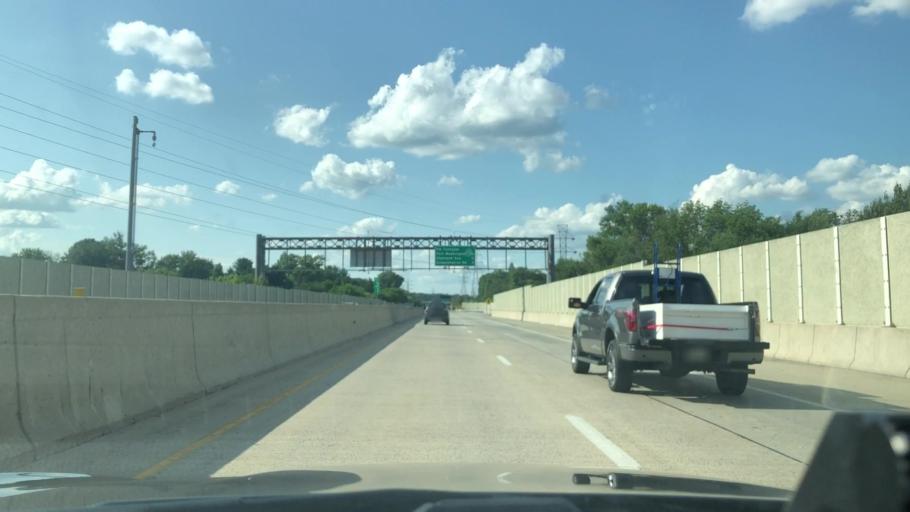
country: US
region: Pennsylvania
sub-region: Montgomery County
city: Flourtown
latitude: 40.1130
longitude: -75.2009
